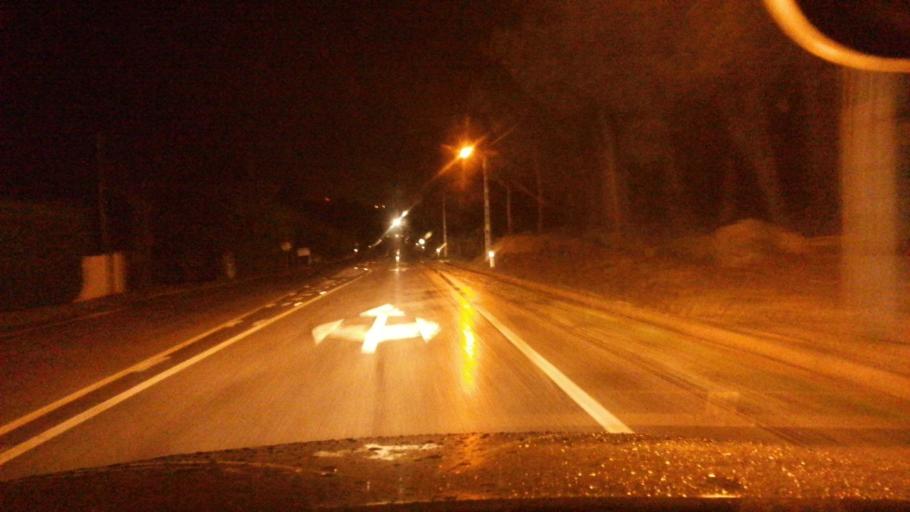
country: PT
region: Viseu
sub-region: Sernancelhe
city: Sernancelhe
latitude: 40.9303
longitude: -7.4361
